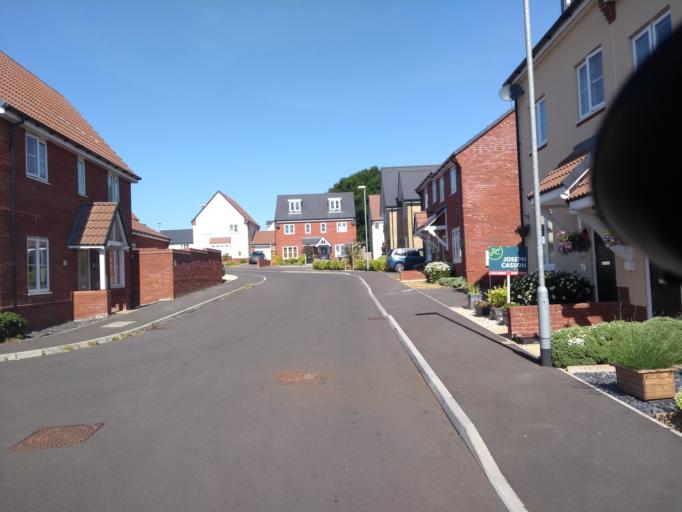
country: GB
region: England
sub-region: Somerset
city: Bridgwater
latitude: 51.1135
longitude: -3.0149
